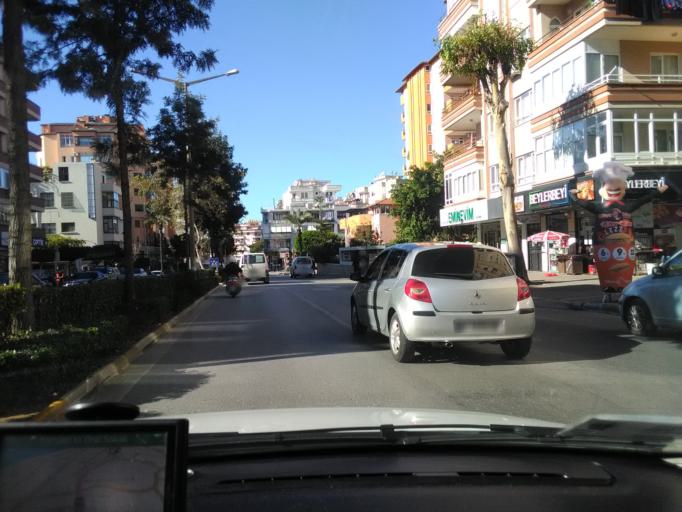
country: TR
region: Antalya
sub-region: Alanya
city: Alanya
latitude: 36.5474
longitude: 31.9960
